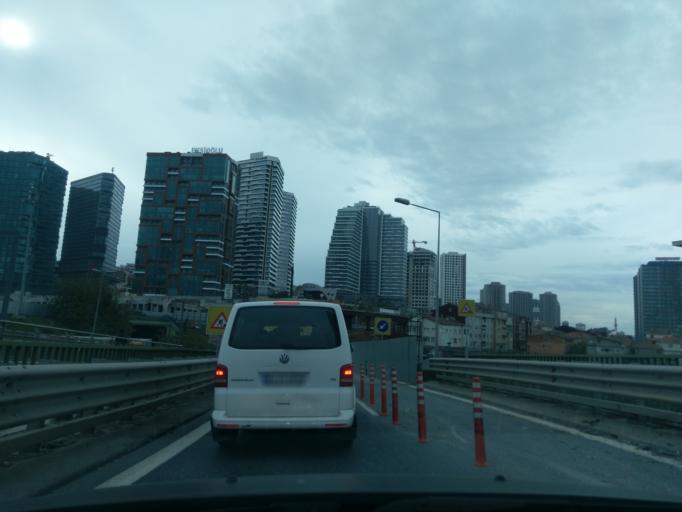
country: TR
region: Istanbul
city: UEskuedar
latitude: 40.9991
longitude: 29.0553
